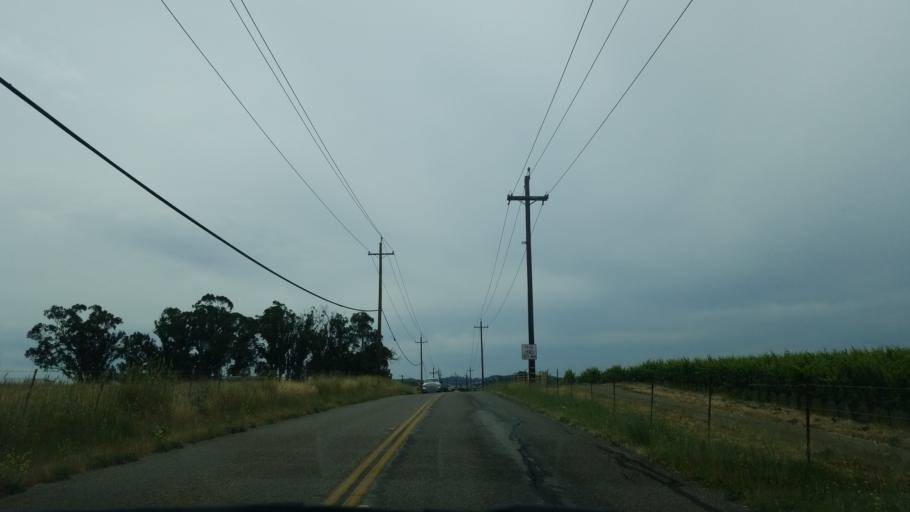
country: US
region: California
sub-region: San Luis Obispo County
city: San Luis Obispo
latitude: 35.2309
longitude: -120.6011
